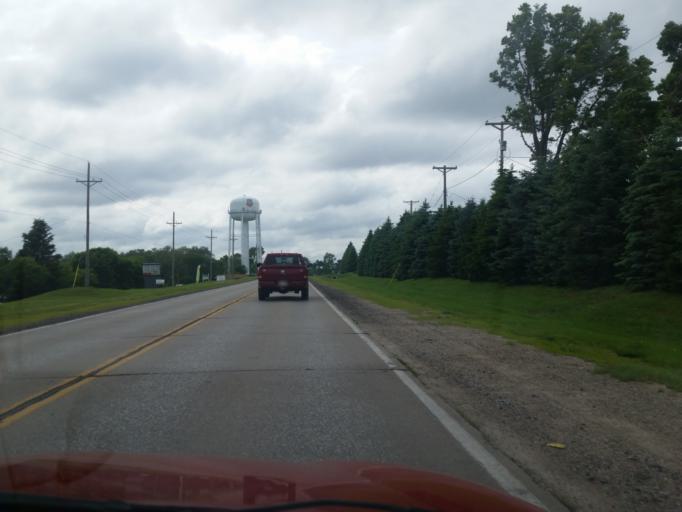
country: US
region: Nebraska
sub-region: Sarpy County
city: Offutt Air Force Base
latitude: 41.1201
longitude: -95.9526
